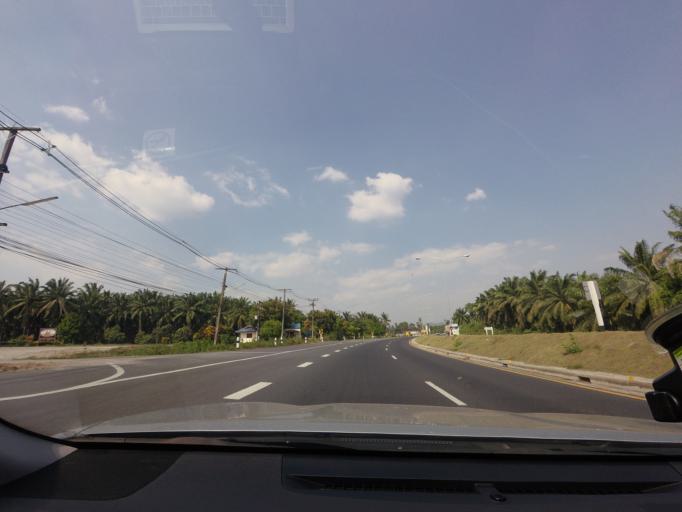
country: TH
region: Phangnga
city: Thap Put
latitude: 8.5685
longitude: 98.7378
